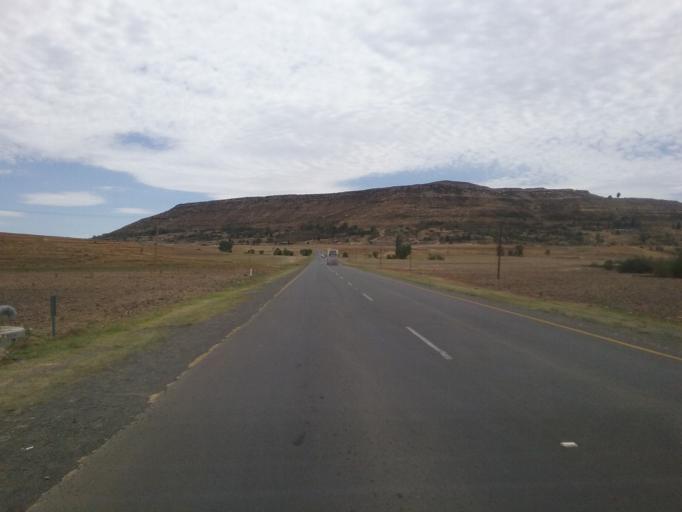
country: LS
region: Maseru
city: Nako
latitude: -29.6159
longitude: 27.4990
